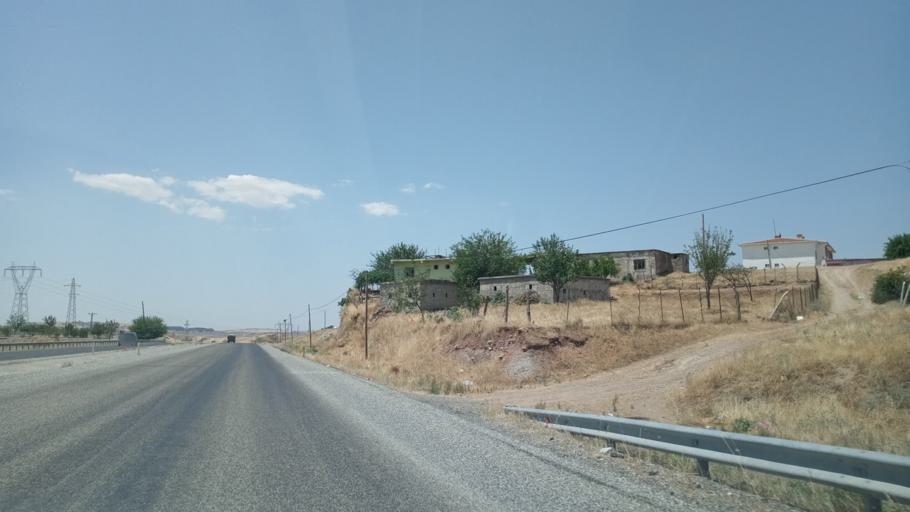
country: TR
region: Batman
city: Kozluk
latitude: 38.1671
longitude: 41.4291
